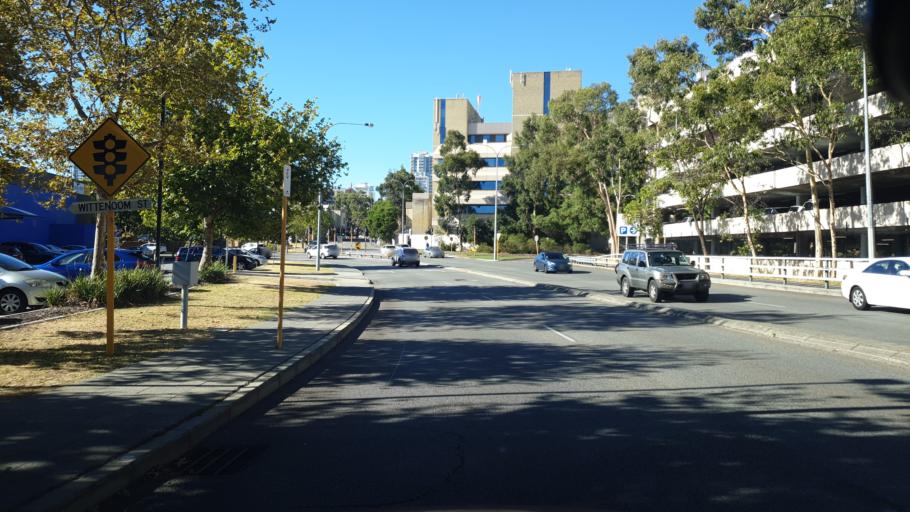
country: AU
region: Western Australia
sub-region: Cambridge
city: Perth
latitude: -31.9521
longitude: 115.8679
